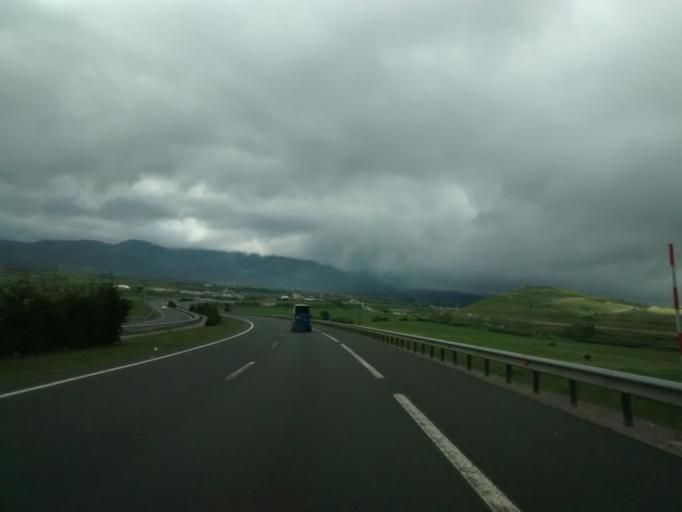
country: ES
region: Cantabria
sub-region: Provincia de Cantabria
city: Villaescusa
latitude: 42.9635
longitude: -4.1557
